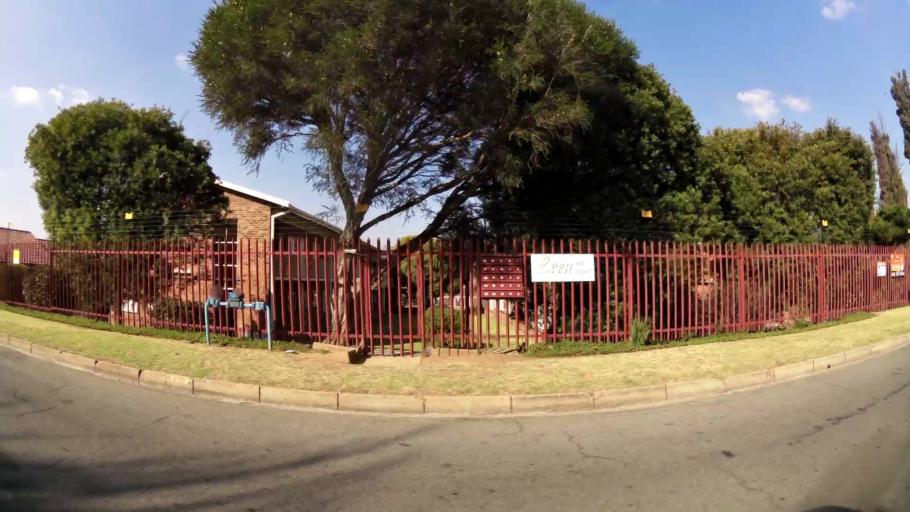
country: ZA
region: Gauteng
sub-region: City of Johannesburg Metropolitan Municipality
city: Modderfontein
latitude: -26.0922
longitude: 28.2166
